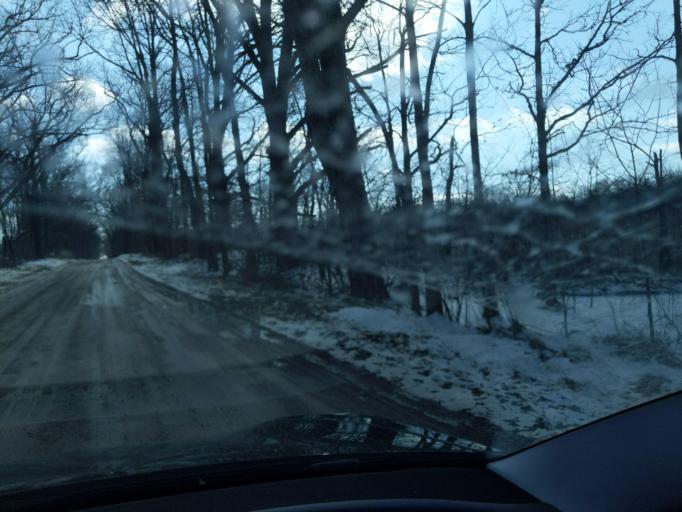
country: US
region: Michigan
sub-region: Livingston County
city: Fowlerville
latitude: 42.5661
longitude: -84.0887
